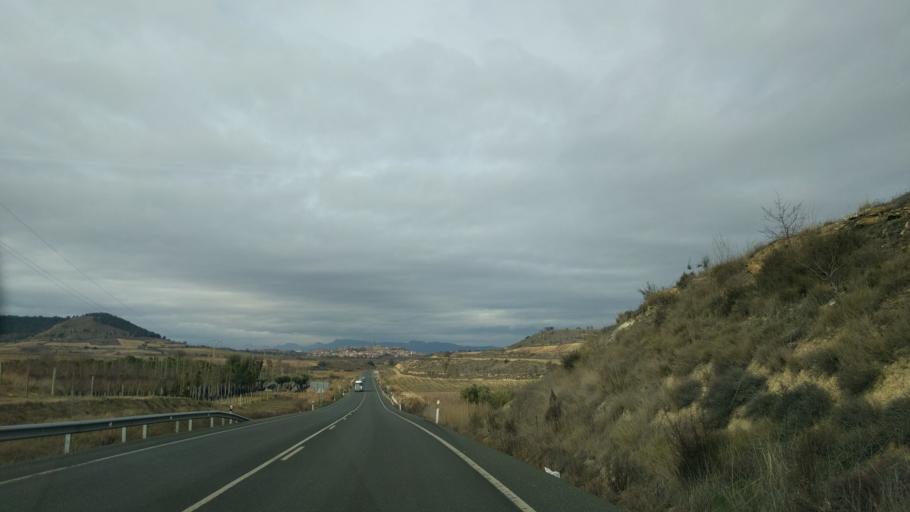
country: ES
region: La Rioja
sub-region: Provincia de La Rioja
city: San Asensio
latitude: 42.5233
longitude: -2.7507
